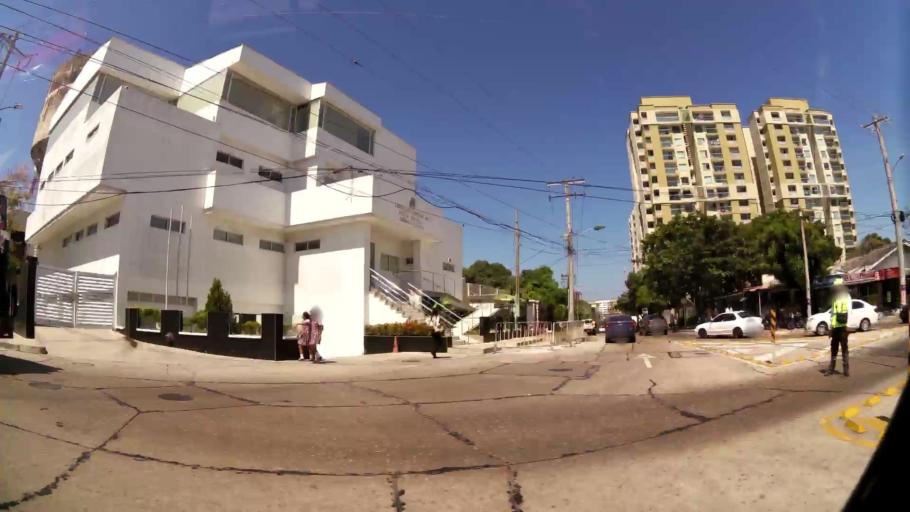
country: CO
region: Atlantico
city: Barranquilla
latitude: 10.9856
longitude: -74.8126
